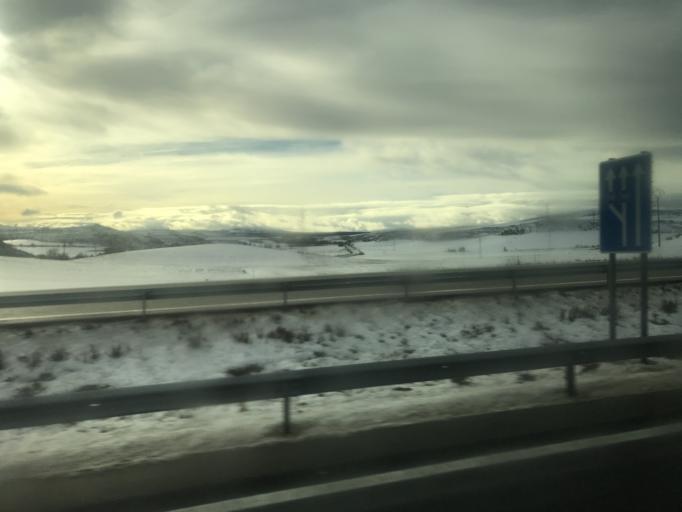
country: ES
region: Castille and Leon
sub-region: Provincia de Burgos
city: Monasterio de Rodilla
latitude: 42.4569
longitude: -3.4544
